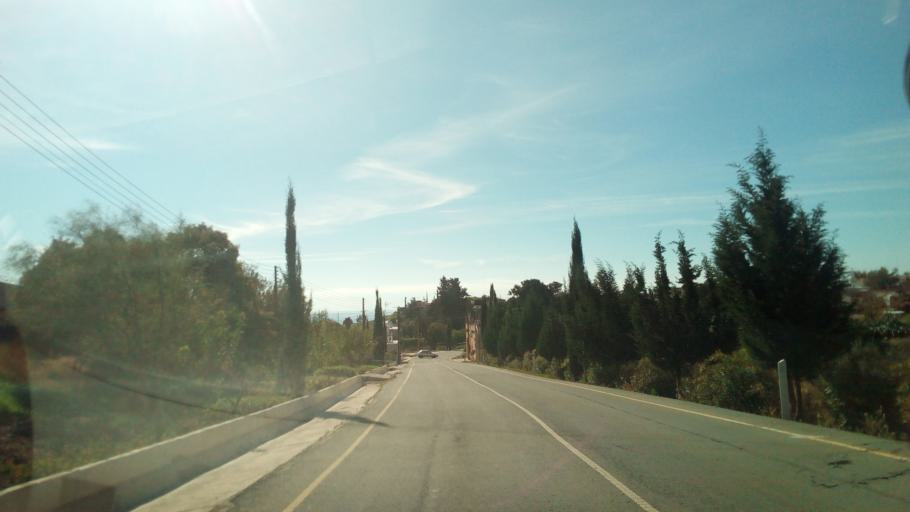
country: CY
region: Limassol
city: Pissouri
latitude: 34.7098
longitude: 32.5777
